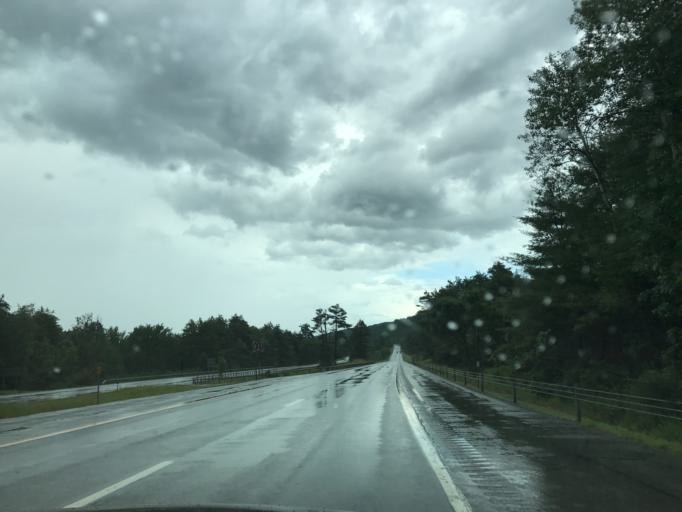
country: US
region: New York
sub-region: Warren County
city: Warrensburg
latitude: 43.4933
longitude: -73.7507
